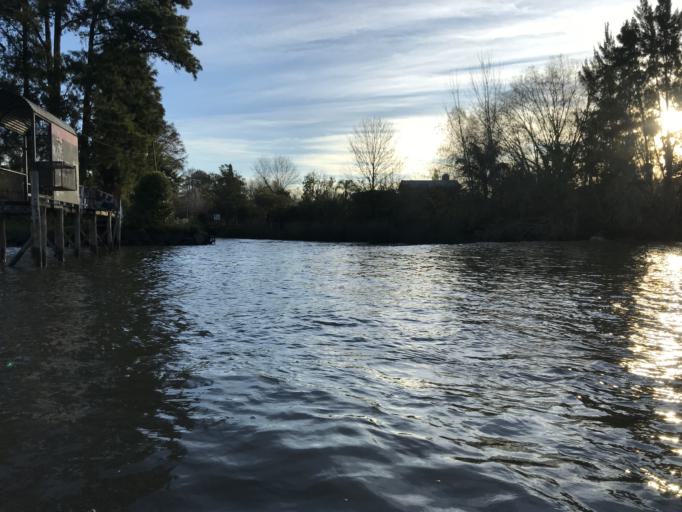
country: AR
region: Buenos Aires
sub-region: Partido de Tigre
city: Tigre
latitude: -34.3962
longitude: -58.5727
